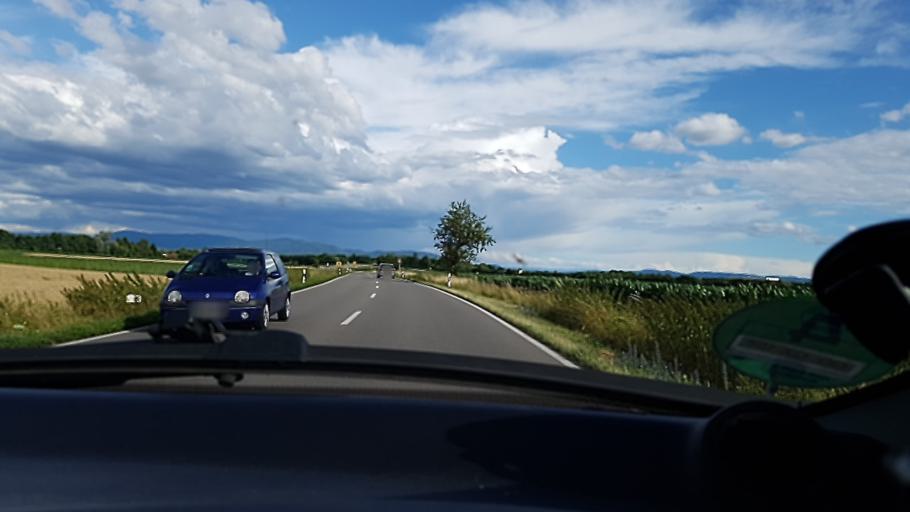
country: DE
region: Baden-Wuerttemberg
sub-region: Freiburg Region
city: Willstatt
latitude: 48.5526
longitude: 7.8807
